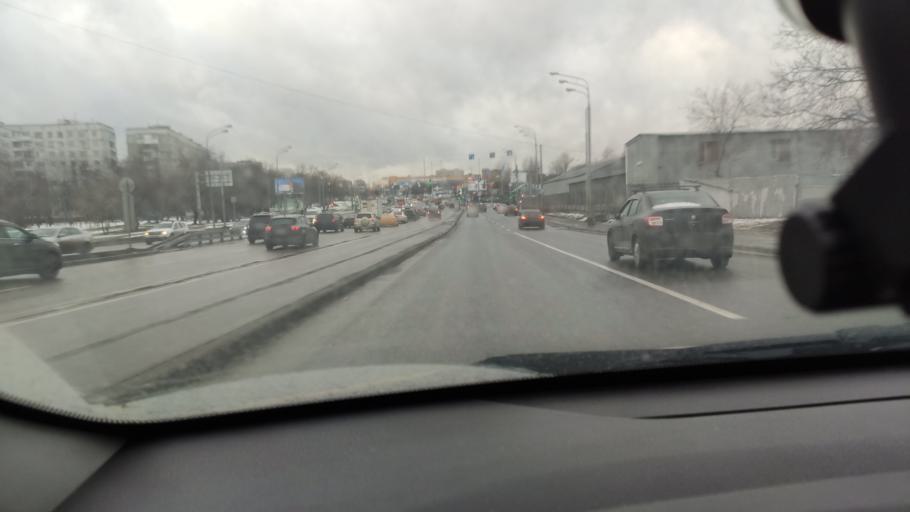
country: RU
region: Moskovskaya
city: Biryulevo Zapadnoye
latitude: 55.6065
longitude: 37.6275
